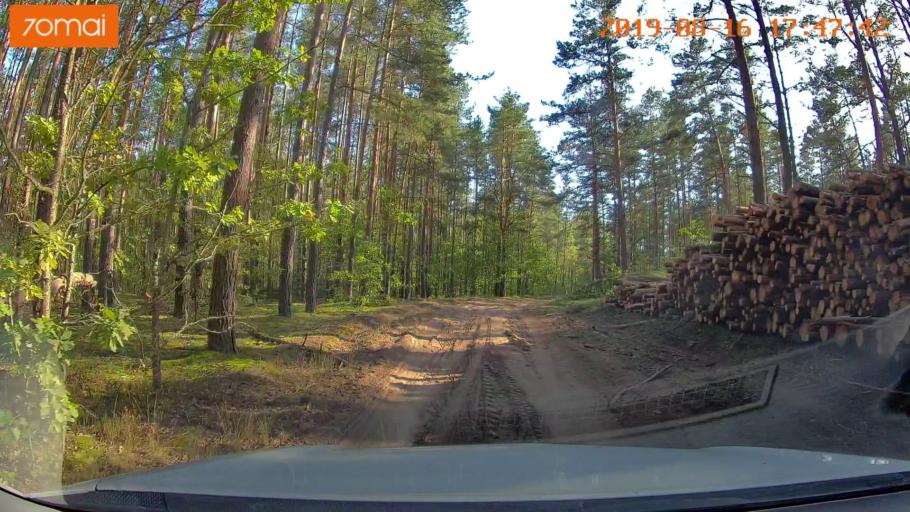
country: BY
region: Mogilev
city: Asipovichy
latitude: 53.2295
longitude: 28.6650
